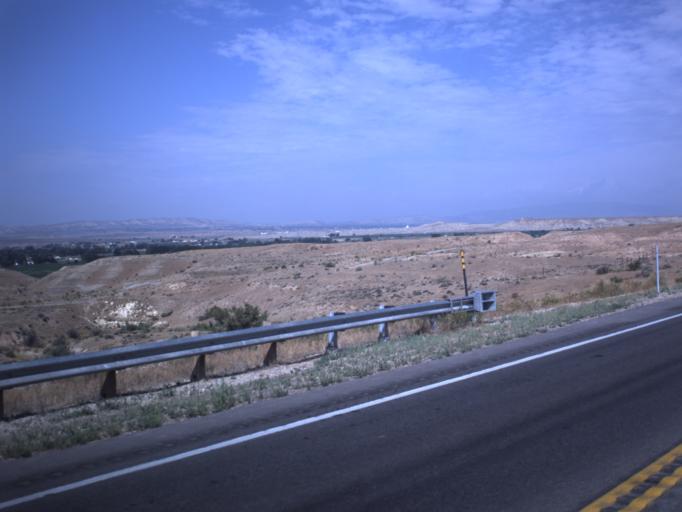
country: US
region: Utah
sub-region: Uintah County
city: Naples
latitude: 40.3643
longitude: -109.3213
